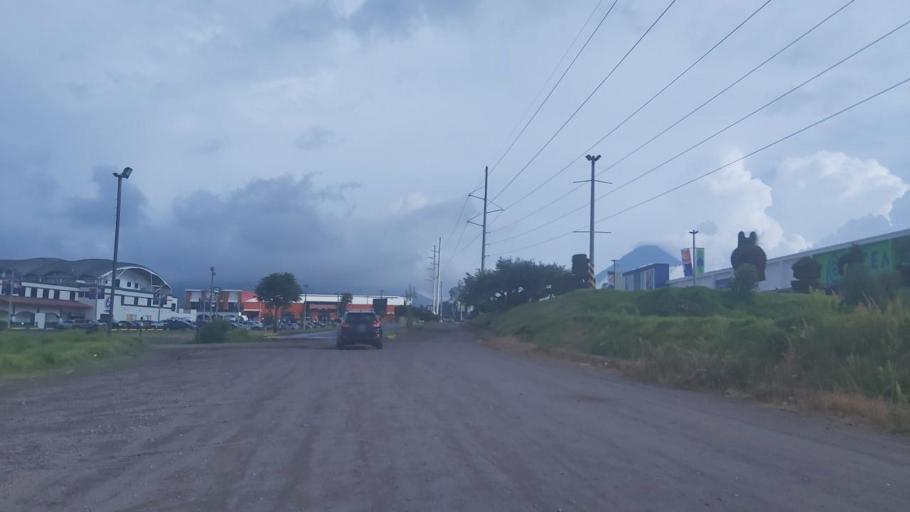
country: GT
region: Quetzaltenango
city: Quetzaltenango
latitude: 14.8493
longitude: -91.5397
